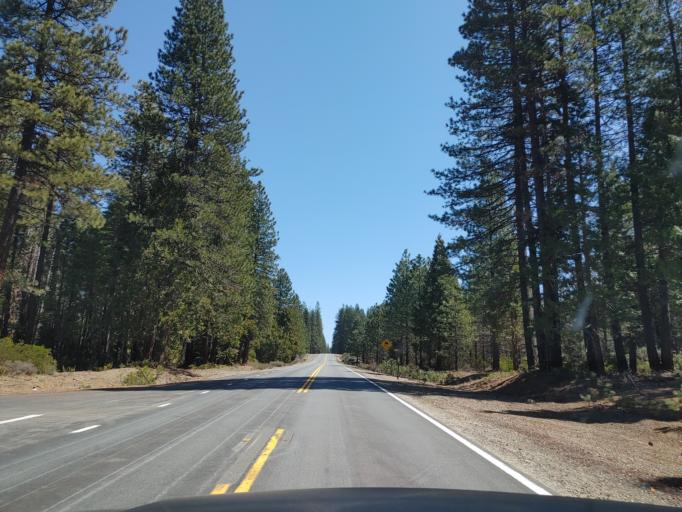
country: US
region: California
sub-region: Siskiyou County
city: McCloud
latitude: 41.2659
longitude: -121.9272
